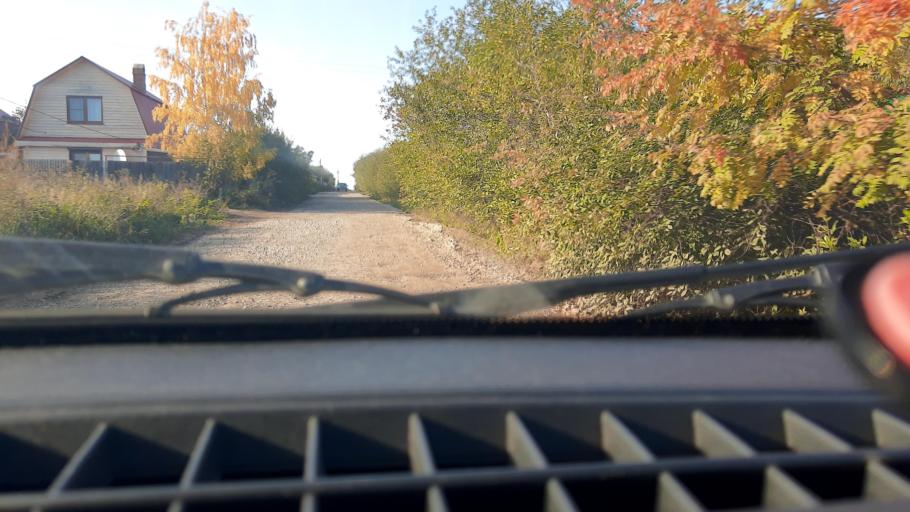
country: RU
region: Bashkortostan
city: Avdon
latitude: 54.5753
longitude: 55.7330
